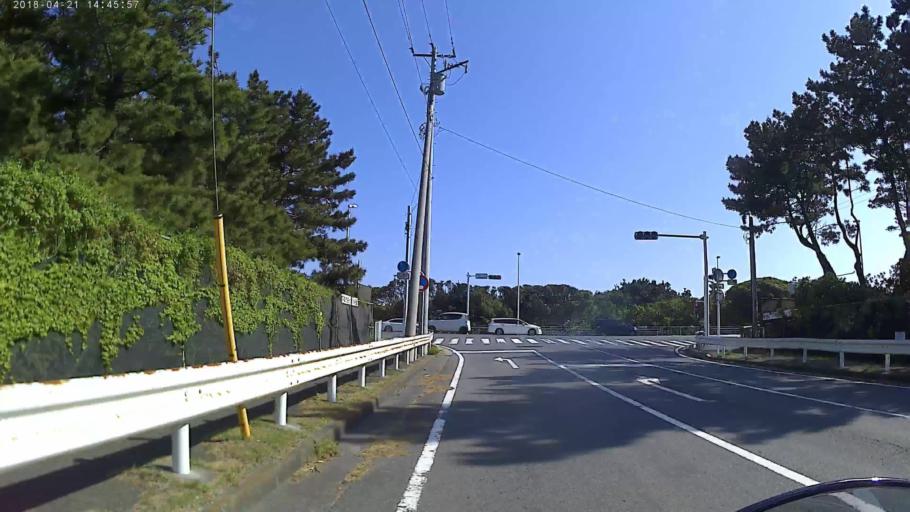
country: JP
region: Kanagawa
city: Hiratsuka
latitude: 35.3161
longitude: 139.3479
